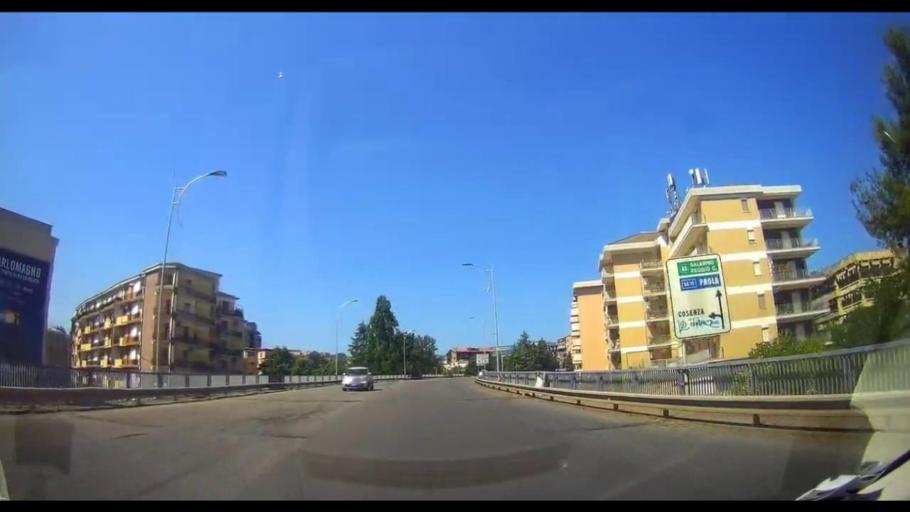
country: IT
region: Calabria
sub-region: Provincia di Cosenza
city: Cosenza
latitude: 39.3113
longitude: 16.2539
